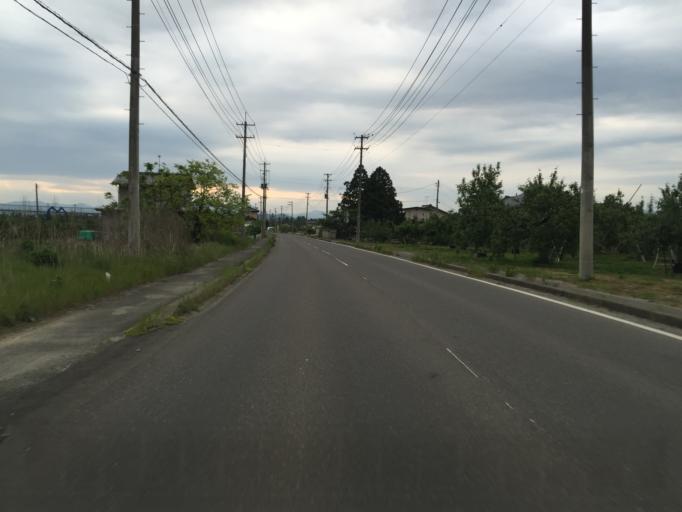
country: JP
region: Fukushima
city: Fukushima-shi
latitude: 37.8135
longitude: 140.4637
